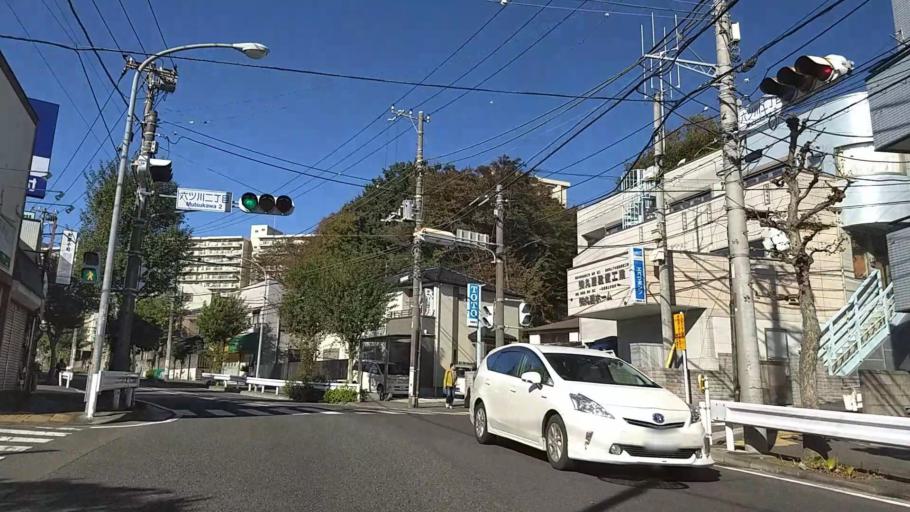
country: JP
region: Kanagawa
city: Yokohama
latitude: 35.4271
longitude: 139.5811
